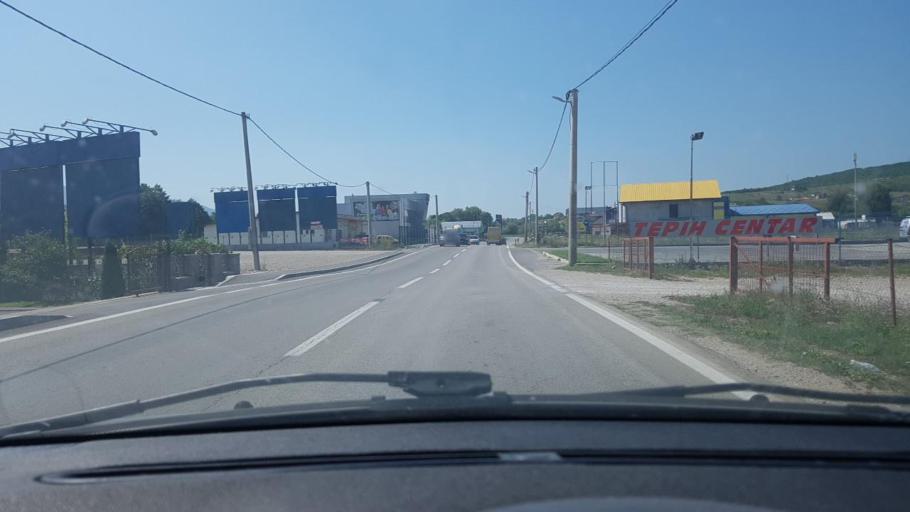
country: BA
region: Federation of Bosnia and Herzegovina
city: Bihac
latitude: 44.7951
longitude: 15.9213
